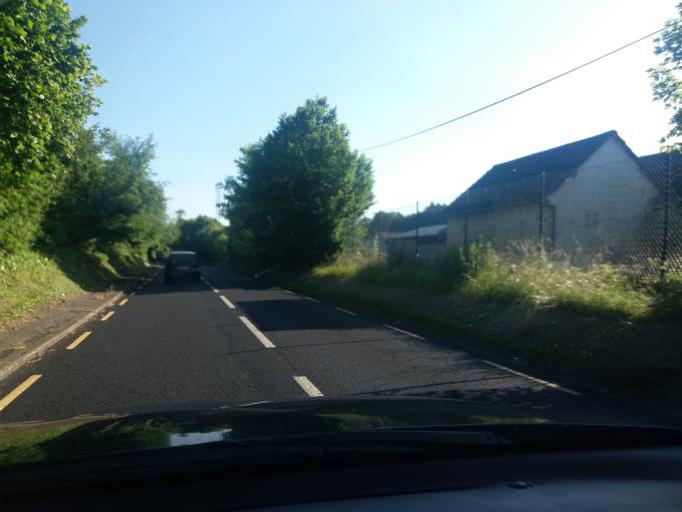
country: IE
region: Leinster
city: Lucan
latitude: 53.3656
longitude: -6.4389
